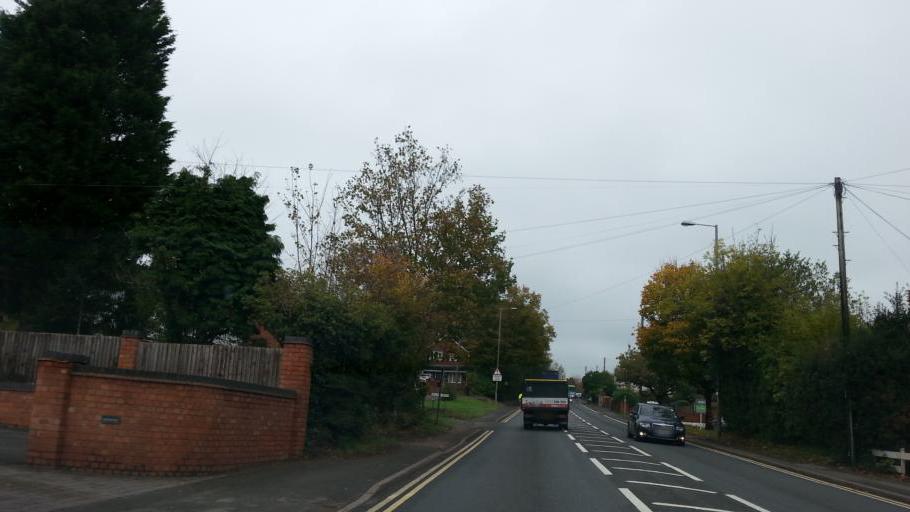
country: GB
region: England
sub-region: Worcestershire
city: Bromsgrove
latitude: 52.3517
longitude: -2.0477
